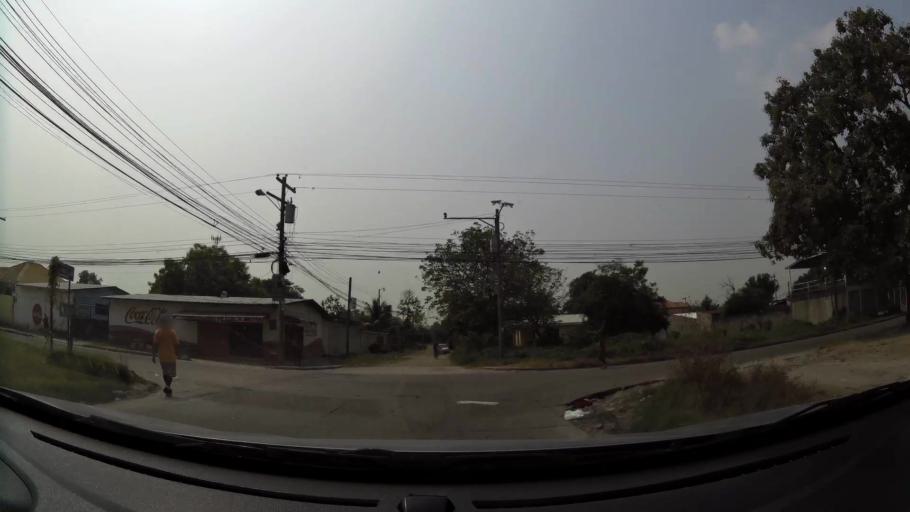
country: HN
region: Cortes
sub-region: San Pedro Sula
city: Pena Blanca
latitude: 15.5491
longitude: -88.0262
